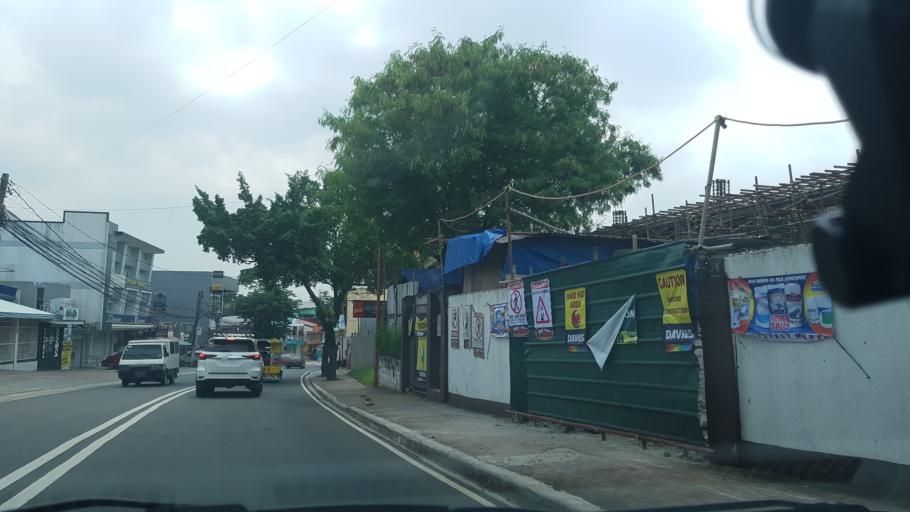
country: PH
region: Calabarzon
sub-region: Province of Rizal
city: Antipolo
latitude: 14.6432
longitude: 121.1217
